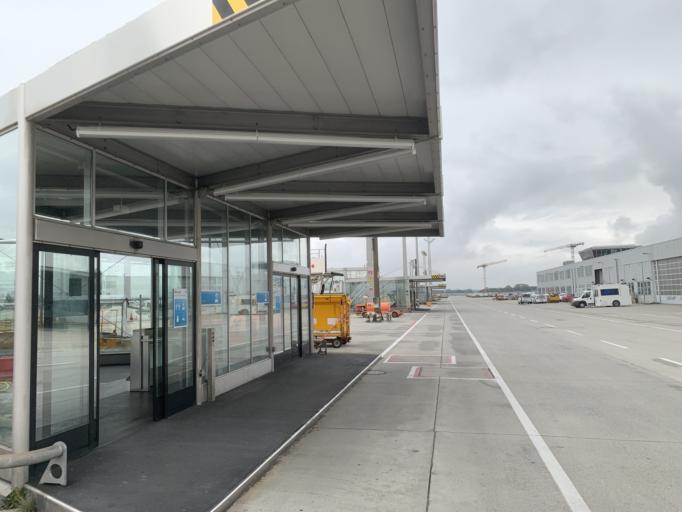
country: DE
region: Bavaria
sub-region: Upper Bavaria
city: Hallbergmoos
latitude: 48.3501
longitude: 11.7805
